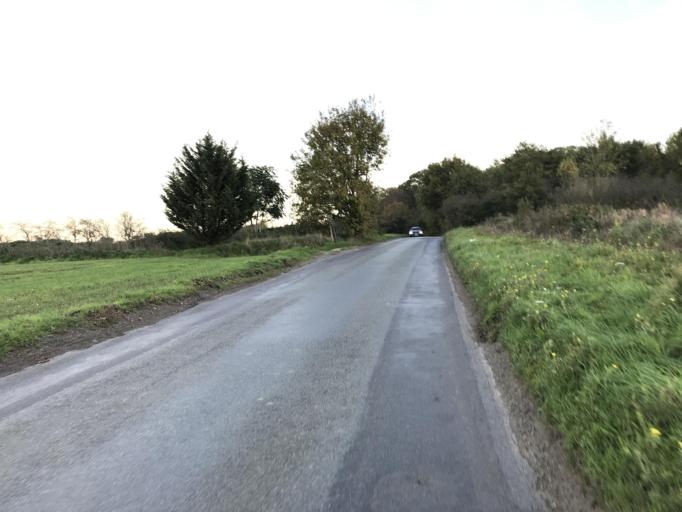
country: FR
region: Ile-de-France
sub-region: Departement de l'Essonne
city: Saulx-les-Chartreux
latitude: 48.6793
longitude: 2.2687
